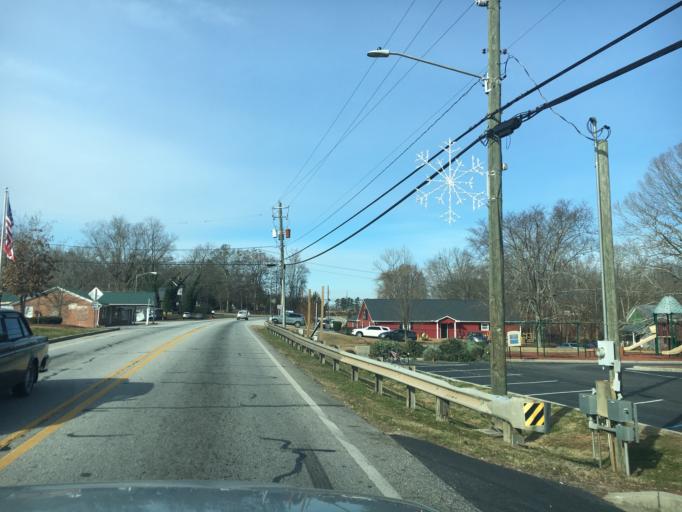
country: US
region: Georgia
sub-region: Jackson County
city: Hoschton
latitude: 34.0974
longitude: -83.7619
